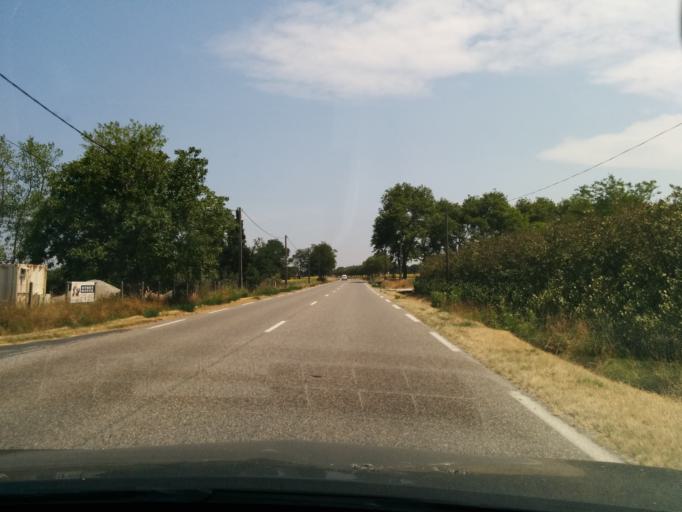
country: FR
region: Languedoc-Roussillon
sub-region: Departement de l'Aude
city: Castelnaudary
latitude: 43.3295
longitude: 1.9172
